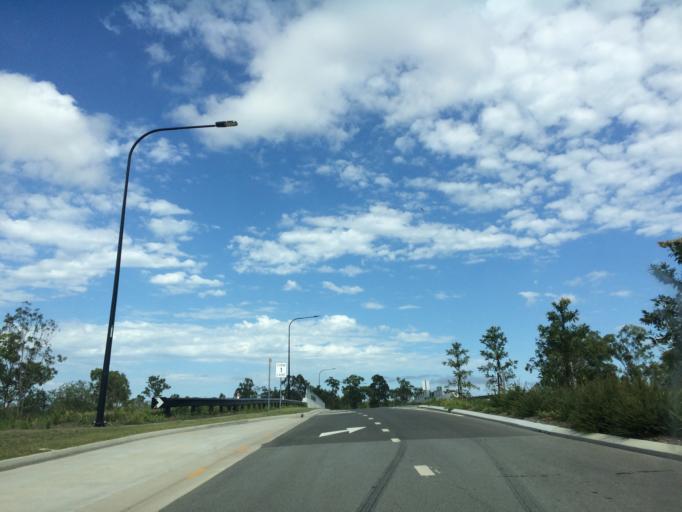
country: AU
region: Queensland
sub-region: Logan
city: North Maclean
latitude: -27.8078
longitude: 152.9492
